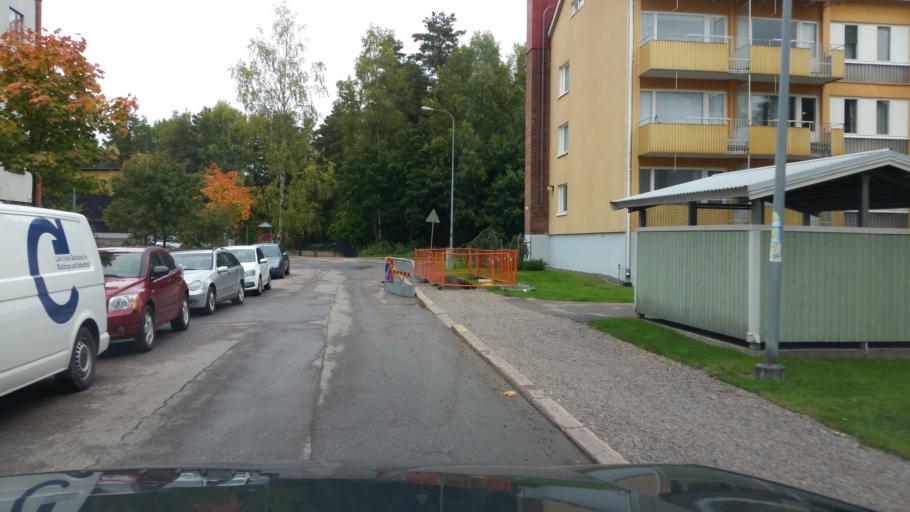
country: FI
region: Uusimaa
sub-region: Helsinki
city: Helsinki
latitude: 60.2130
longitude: 24.8939
